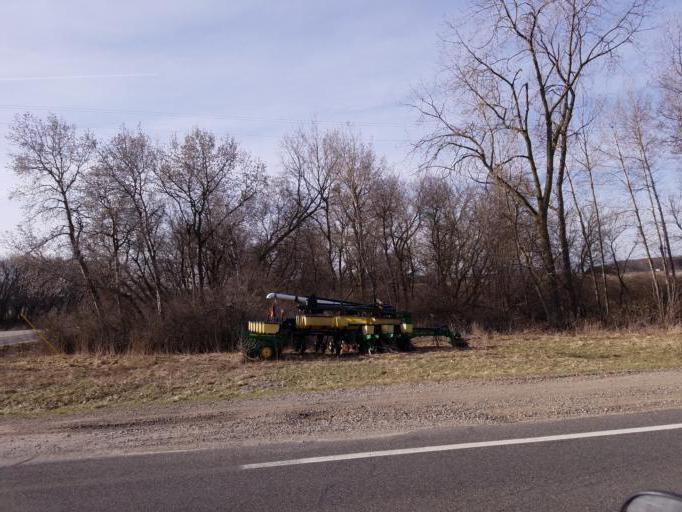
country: US
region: Michigan
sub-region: Montcalm County
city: Lakeview
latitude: 43.4314
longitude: -85.2838
